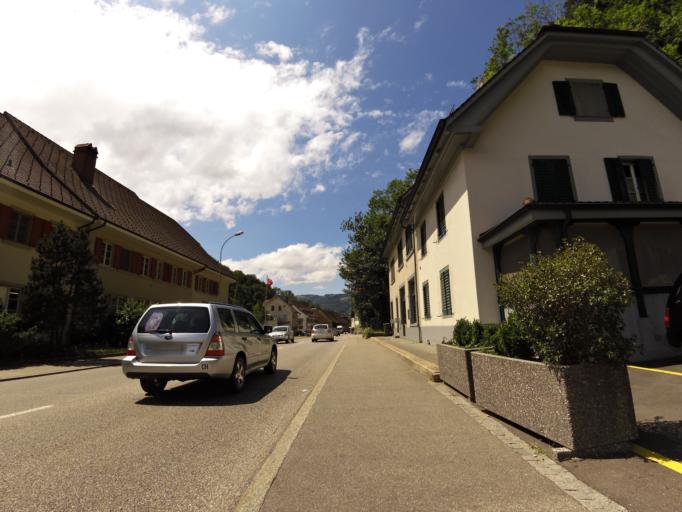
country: CH
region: Solothurn
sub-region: Bezirk Thal
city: Balsthal
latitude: 47.3061
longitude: 7.6923
